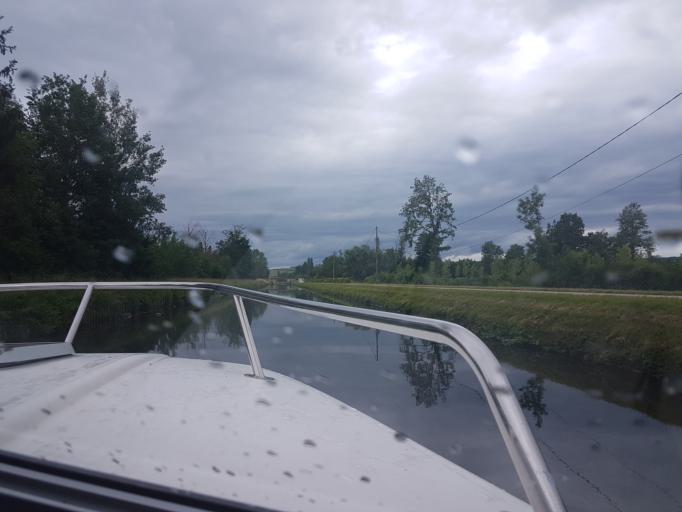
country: FR
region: Bourgogne
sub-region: Departement de l'Yonne
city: Saint-Bris-le-Vineux
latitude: 47.7096
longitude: 3.6364
